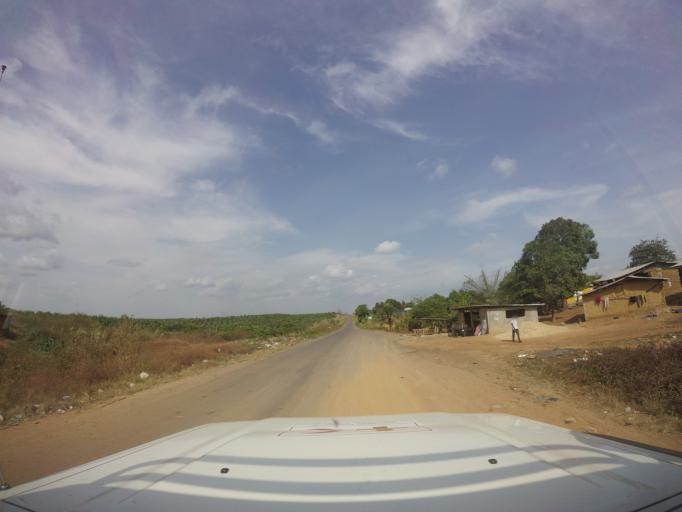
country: LR
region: Bomi
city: Tubmanburg
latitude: 6.7275
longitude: -11.0360
